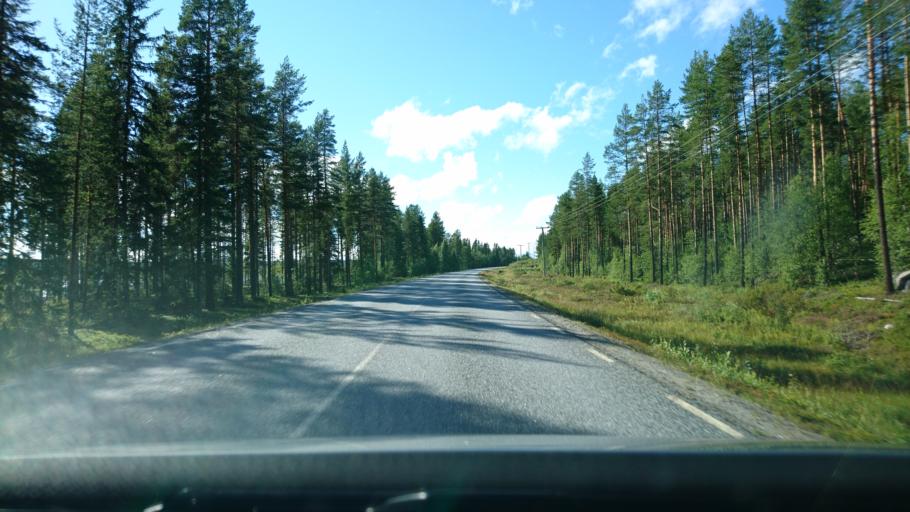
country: SE
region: Vaesterbotten
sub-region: Vilhelmina Kommun
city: Vilhelmina
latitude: 64.3676
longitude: 16.9274
